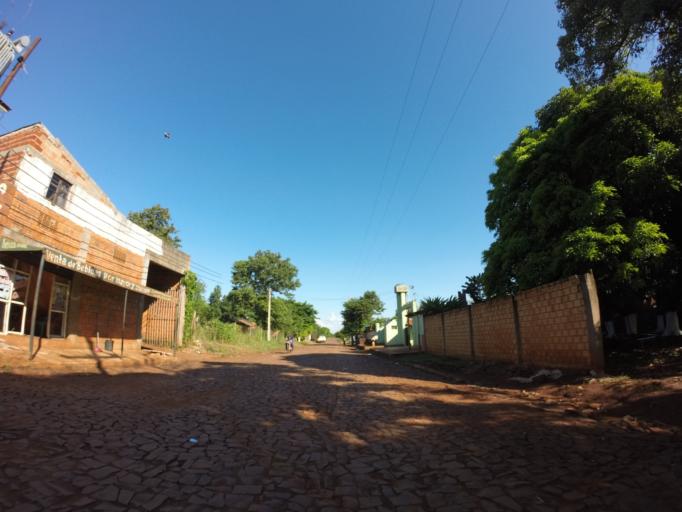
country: PY
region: Alto Parana
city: Ciudad del Este
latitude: -25.3884
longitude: -54.6525
